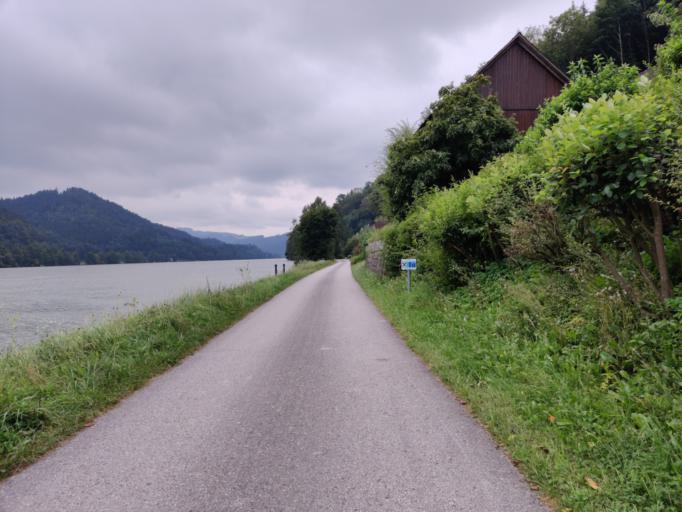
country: AT
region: Lower Austria
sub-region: Politischer Bezirk Melk
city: Nochling
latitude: 48.2213
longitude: 14.9464
